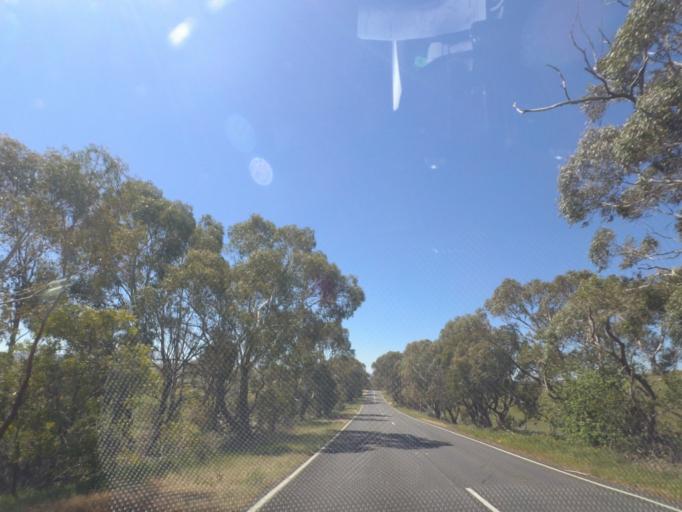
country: AU
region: Victoria
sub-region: Hume
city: Sunbury
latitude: -37.1856
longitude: 144.7412
